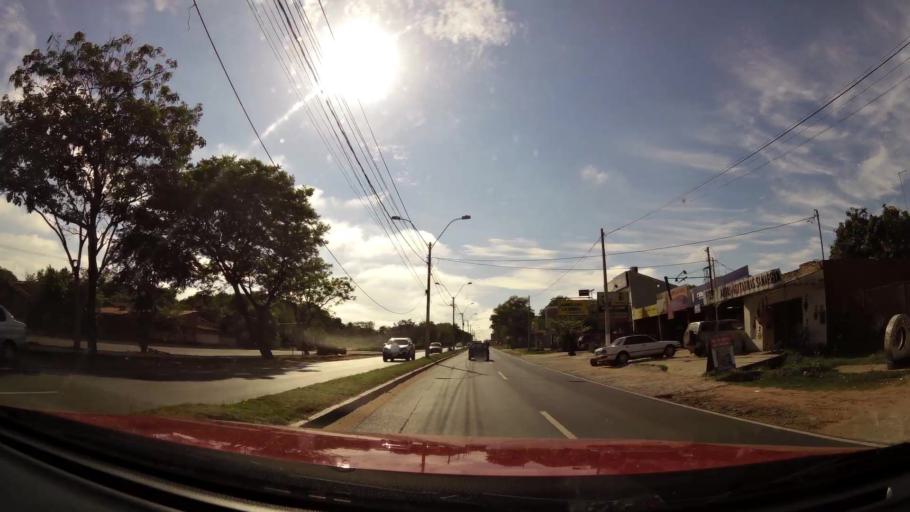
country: PY
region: Central
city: Fernando de la Mora
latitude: -25.2636
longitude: -57.5124
